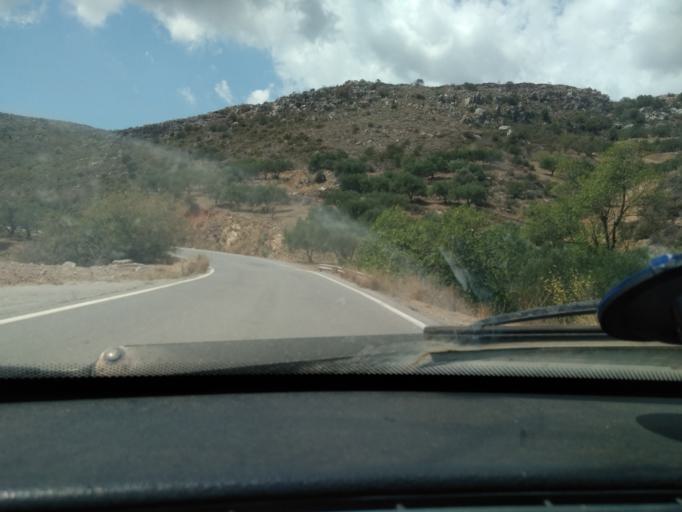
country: GR
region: Crete
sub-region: Nomos Lasithiou
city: Siteia
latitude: 35.1146
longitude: 26.0573
